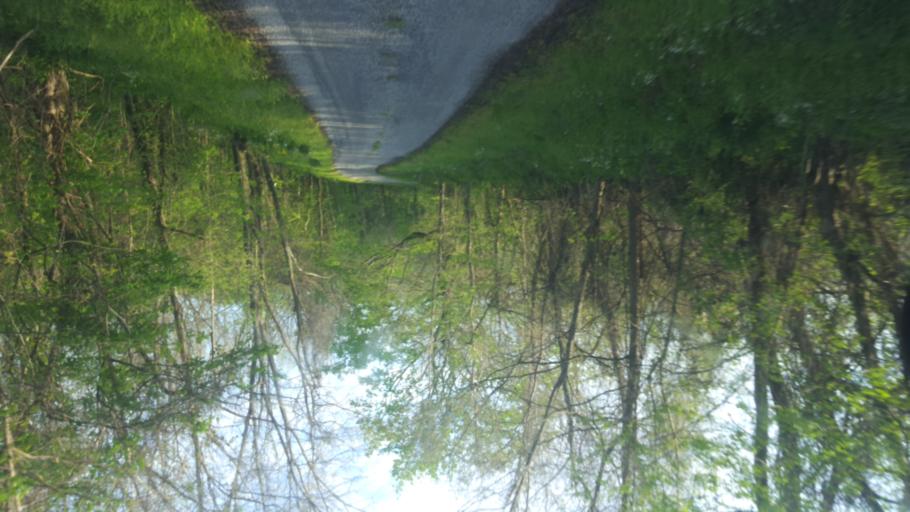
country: US
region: Kentucky
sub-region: Hart County
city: Munfordville
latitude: 37.2462
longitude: -85.9320
